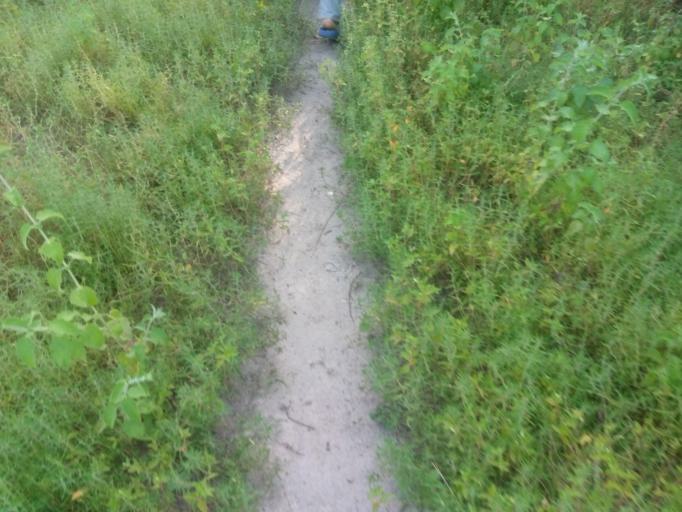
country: GM
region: Western
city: Gunjur
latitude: 13.0385
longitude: -16.7247
